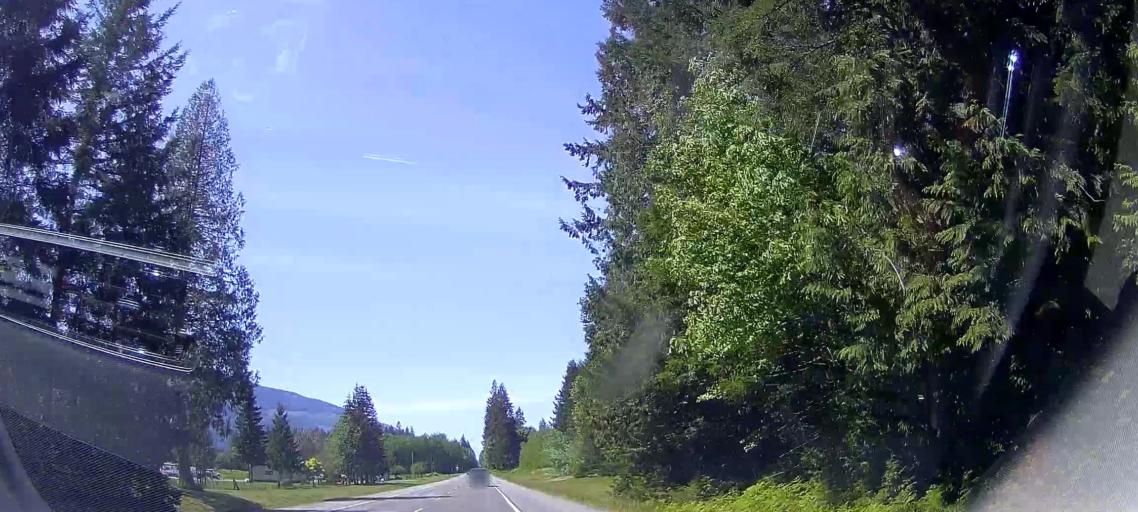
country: US
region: Washington
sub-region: Skagit County
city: Sedro-Woolley
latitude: 48.5379
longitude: -121.8604
